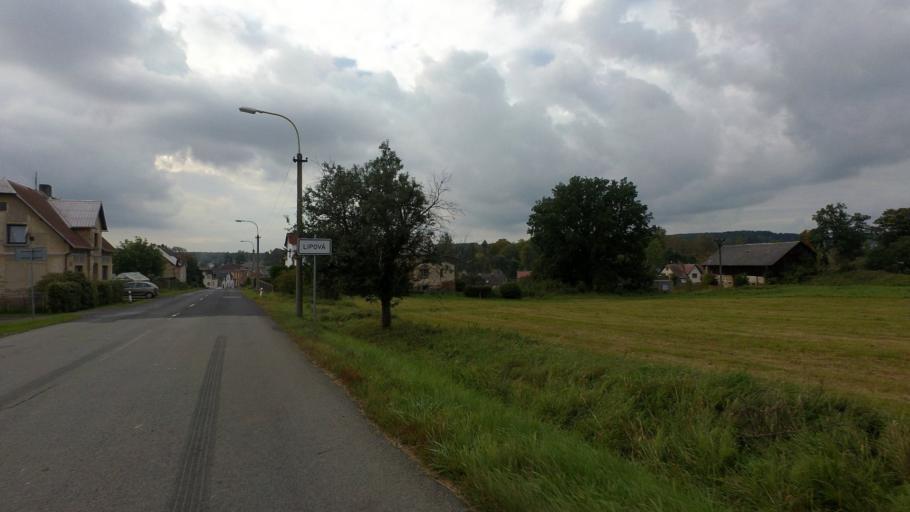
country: CZ
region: Ustecky
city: Velky Senov
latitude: 51.0101
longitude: 14.3630
